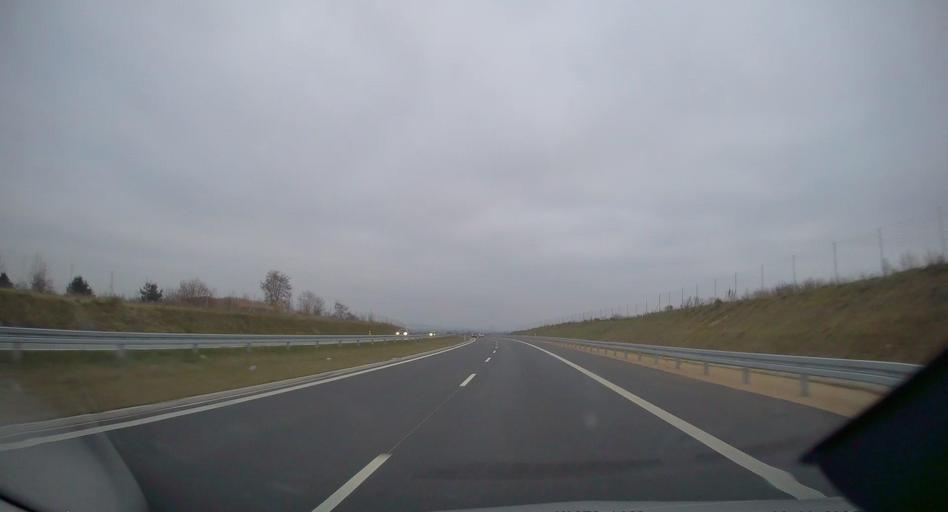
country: PL
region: Silesian Voivodeship
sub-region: Powiat bedzinski
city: Mierzecice
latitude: 50.4294
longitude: 19.1544
